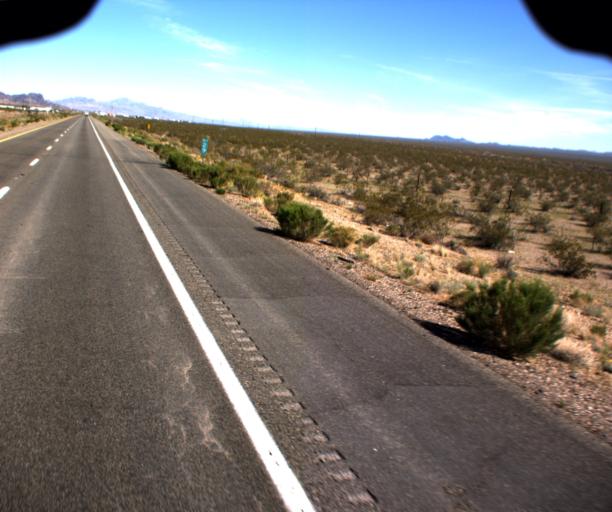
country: US
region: Arizona
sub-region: Mohave County
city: Dolan Springs
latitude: 35.6940
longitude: -114.4712
